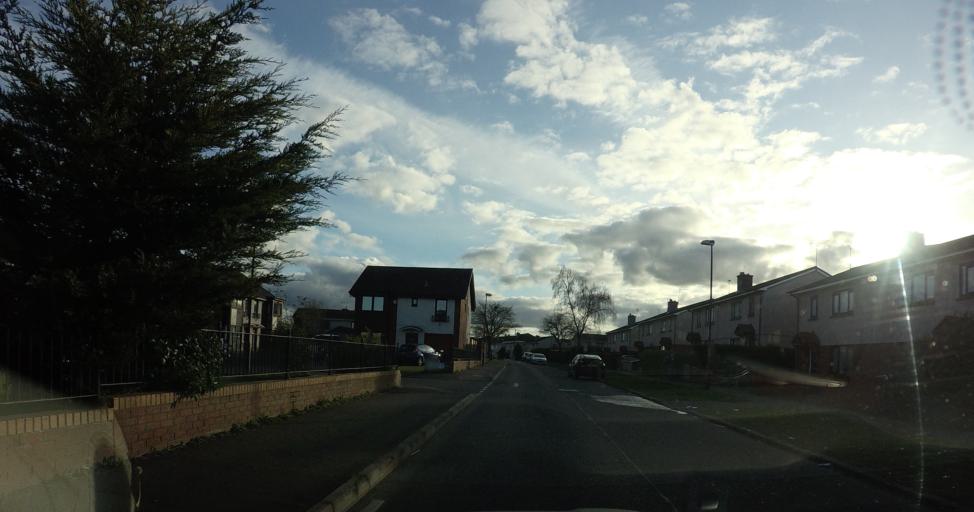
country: GB
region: Scotland
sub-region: Midlothian
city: Loanhead
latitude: 55.8994
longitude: -3.1569
